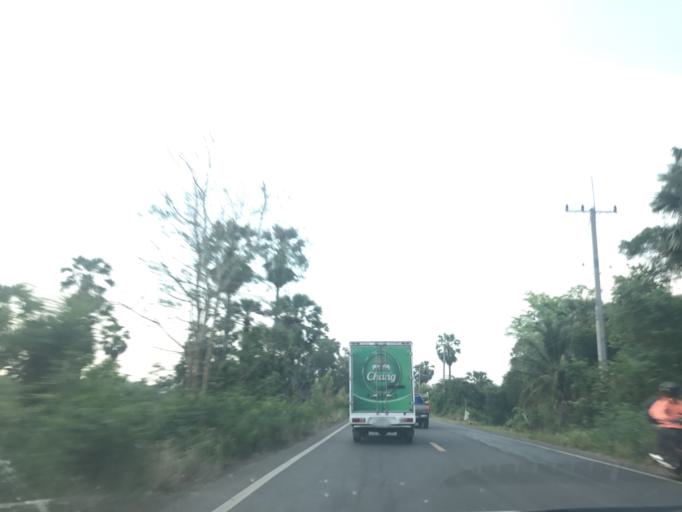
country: TH
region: Buriram
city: Nang Rong
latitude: 14.6100
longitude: 102.7961
